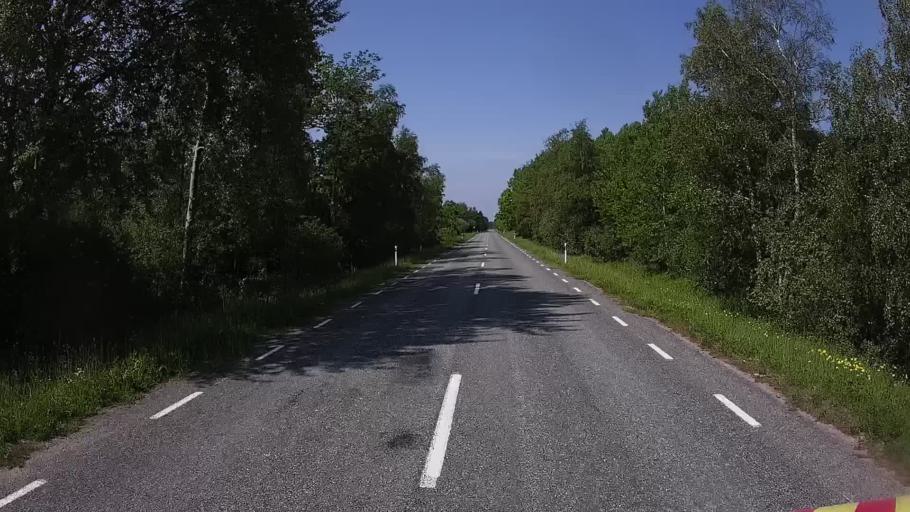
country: EE
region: Saare
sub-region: Kuressaare linn
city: Kuressaare
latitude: 58.3716
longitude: 22.0449
